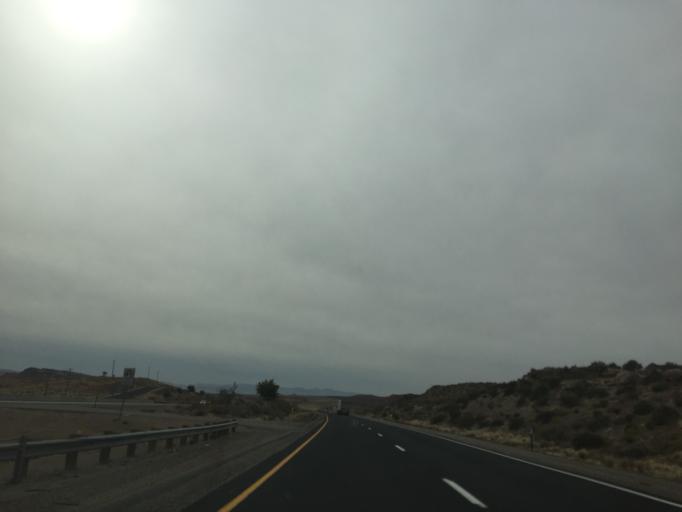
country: US
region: Utah
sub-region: Washington County
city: Toquerville
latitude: 37.2216
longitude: -113.3837
